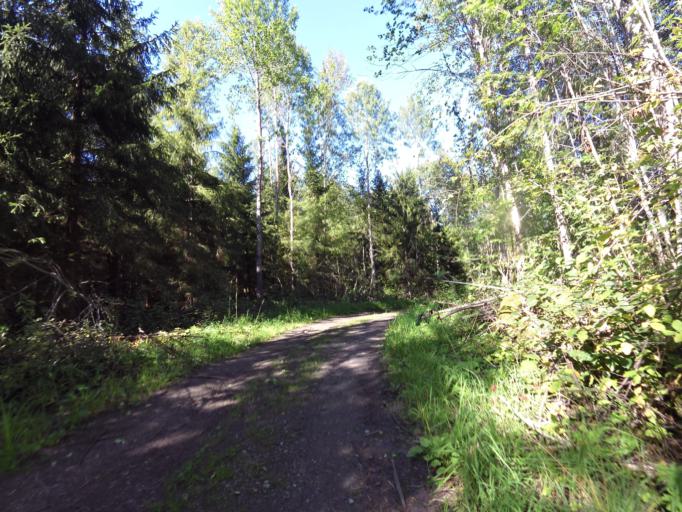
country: SE
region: Gaevleborg
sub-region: Hofors Kommun
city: Hofors
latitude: 60.5248
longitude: 16.4070
